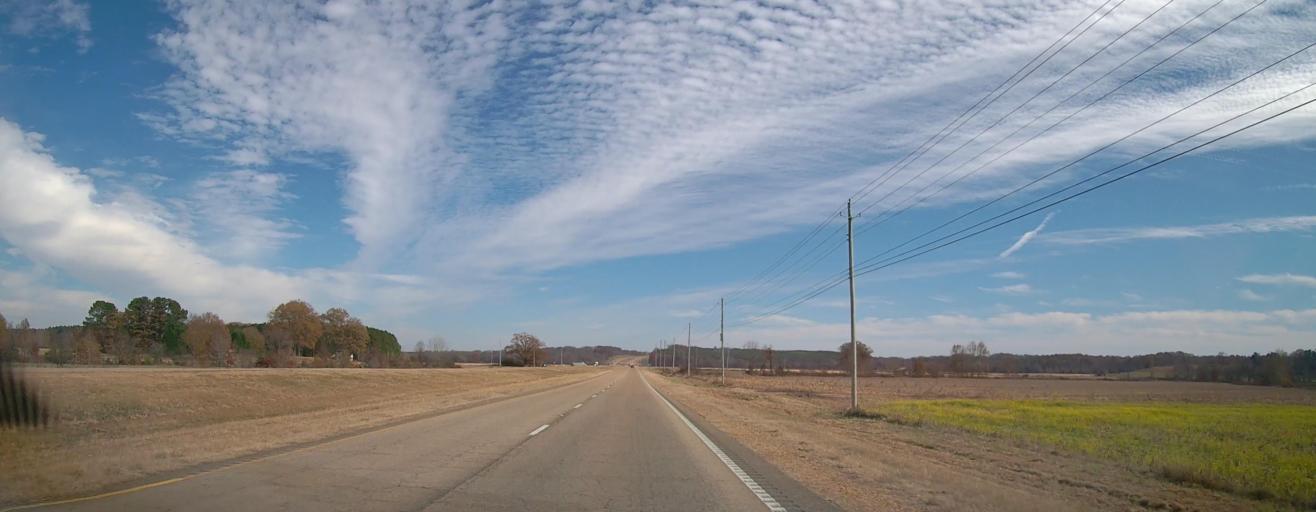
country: US
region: Mississippi
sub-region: Alcorn County
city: Corinth
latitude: 34.9311
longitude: -88.6710
